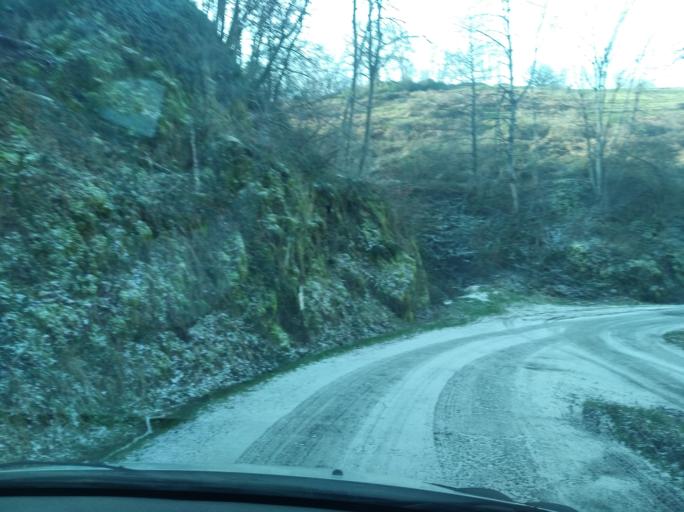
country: FR
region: Rhone-Alpes
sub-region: Departement de la Loire
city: La Pacaudiere
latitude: 46.1685
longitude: 3.7509
